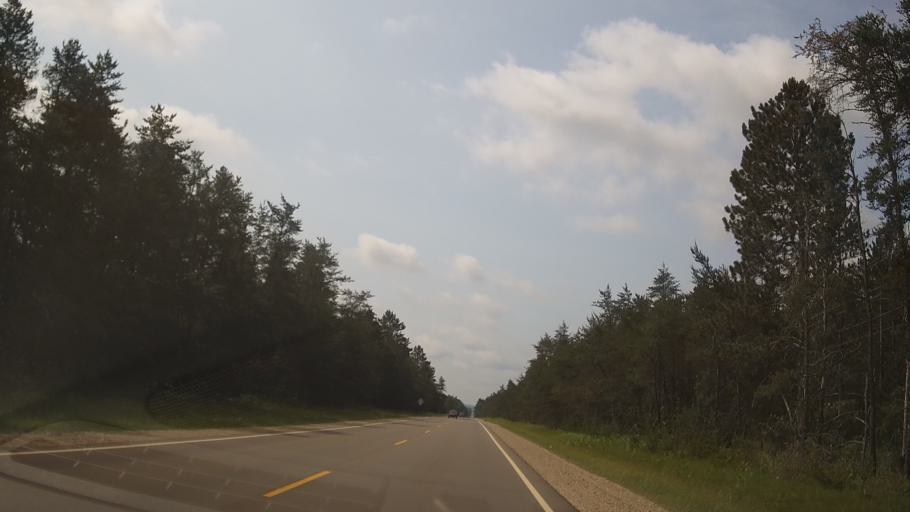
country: US
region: Michigan
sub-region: Roscommon County
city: Saint Helen
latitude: 44.3997
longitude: -84.4104
